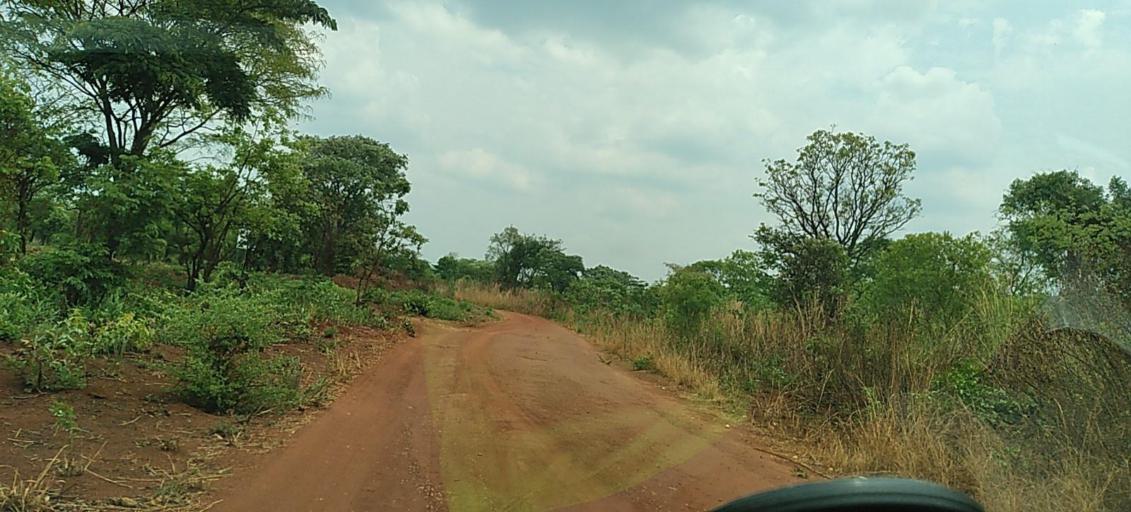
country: ZM
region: North-Western
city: Kansanshi
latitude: -12.0464
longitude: 26.3822
